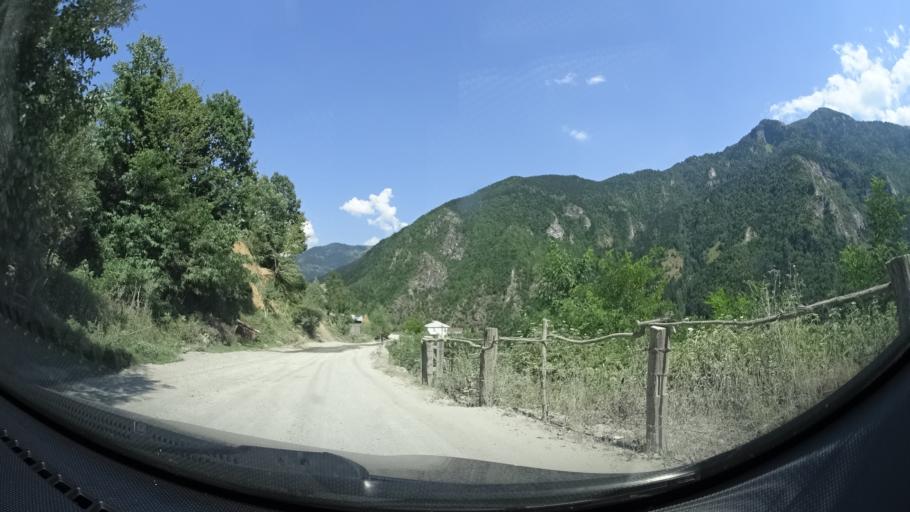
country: GE
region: Ajaria
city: Khulo
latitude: 41.6470
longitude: 42.3194
